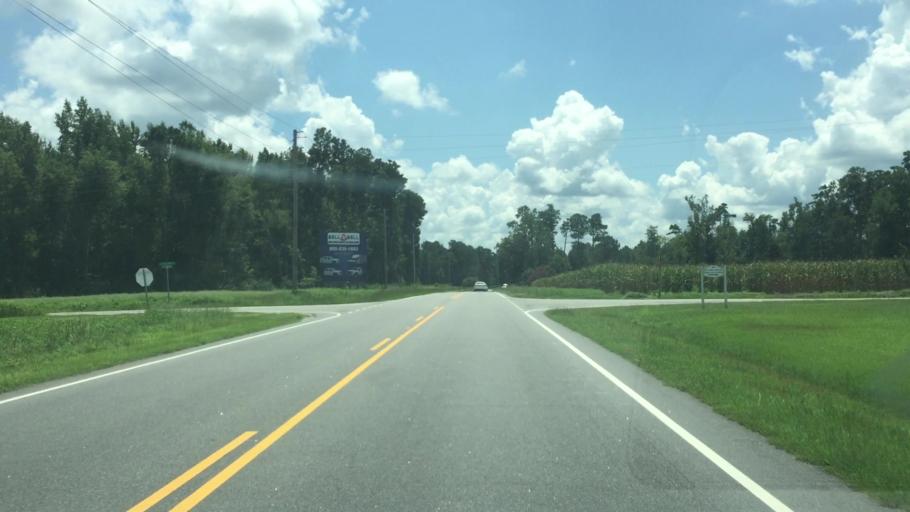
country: US
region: North Carolina
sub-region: Columbus County
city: Tabor City
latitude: 34.2198
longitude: -78.8241
